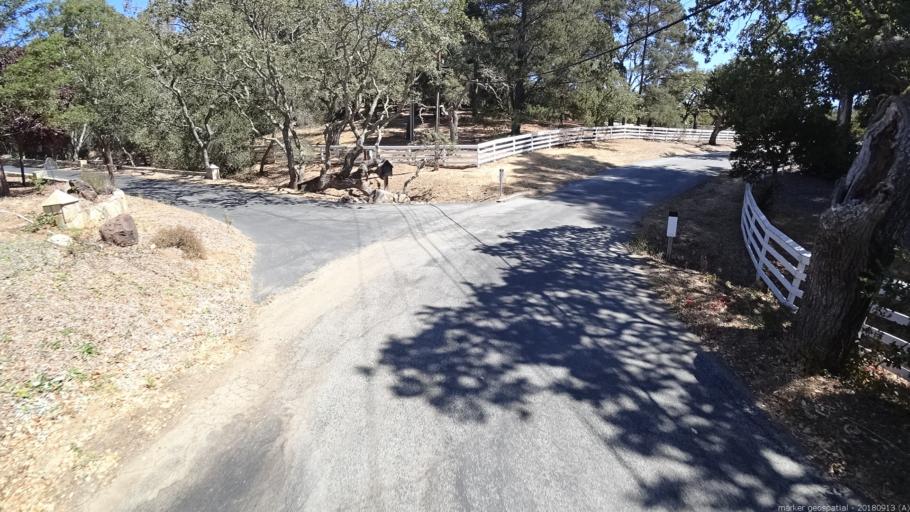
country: US
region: California
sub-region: Monterey County
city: Carmel Valley Village
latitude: 36.5042
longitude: -121.7537
